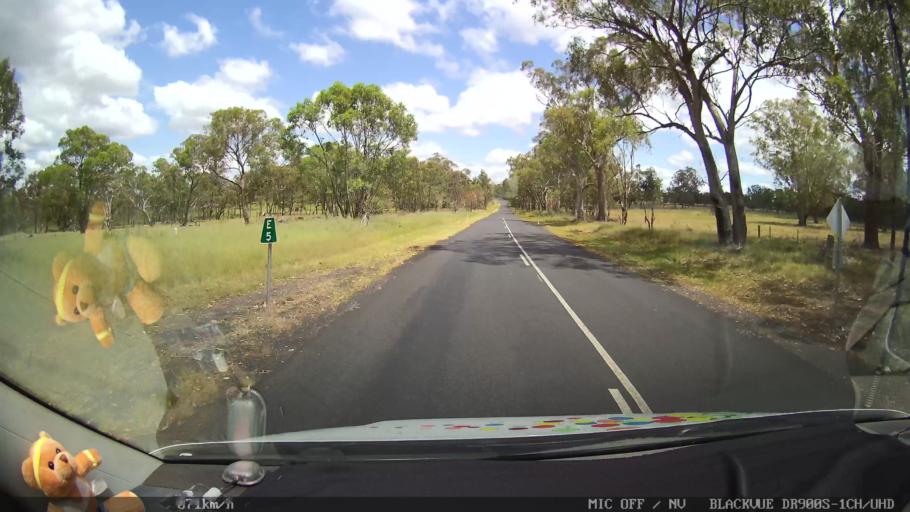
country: AU
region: New South Wales
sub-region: Glen Innes Severn
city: Glen Innes
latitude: -29.4700
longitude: 151.6407
